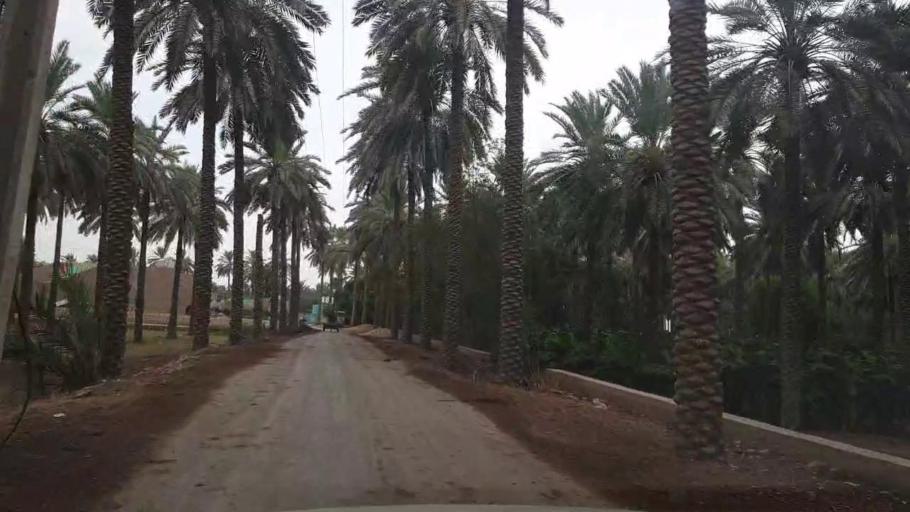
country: PK
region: Sindh
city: Khairpur
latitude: 27.5471
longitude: 68.7525
